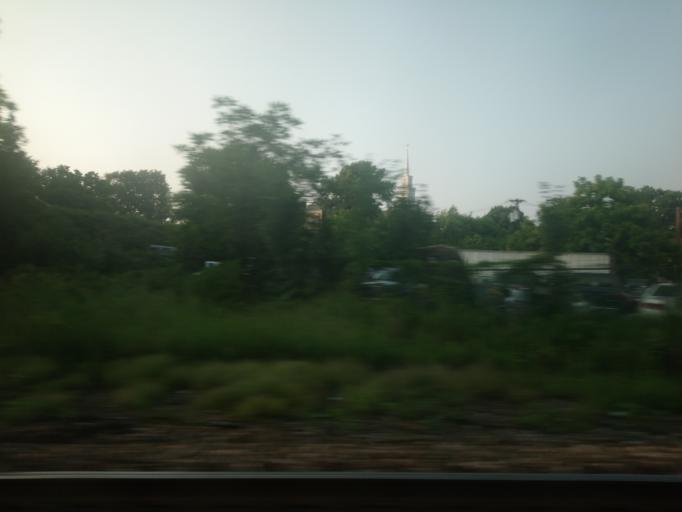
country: US
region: New Jersey
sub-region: Essex County
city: Orange
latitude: 40.7721
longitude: -74.2348
